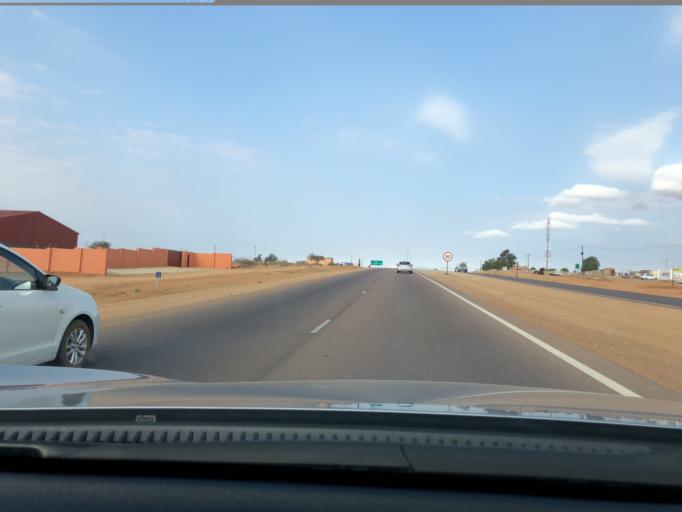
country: ZA
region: Limpopo
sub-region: Capricorn District Municipality
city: Mankoeng
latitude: -23.8902
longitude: 29.6635
